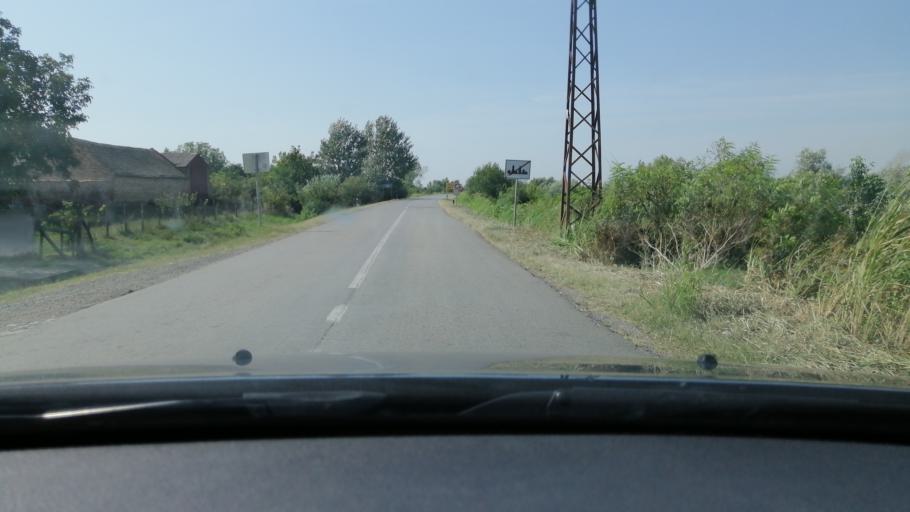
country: RS
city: Tomasevac
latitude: 45.2600
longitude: 20.6170
